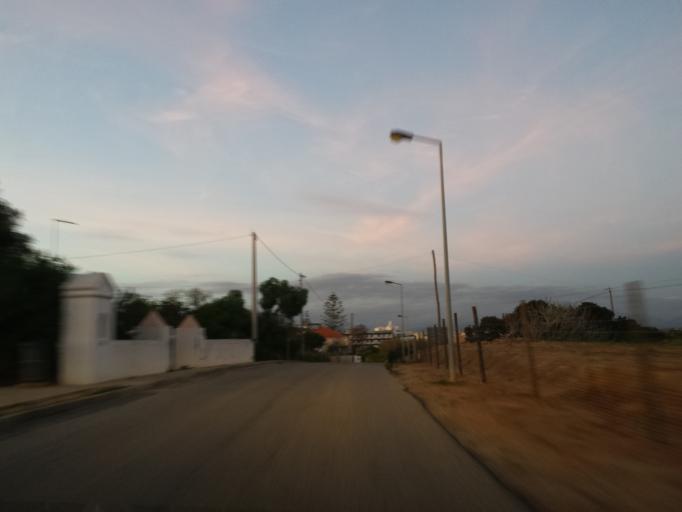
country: PT
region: Faro
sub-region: Lagos
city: Lagos
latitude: 37.0879
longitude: -8.6714
